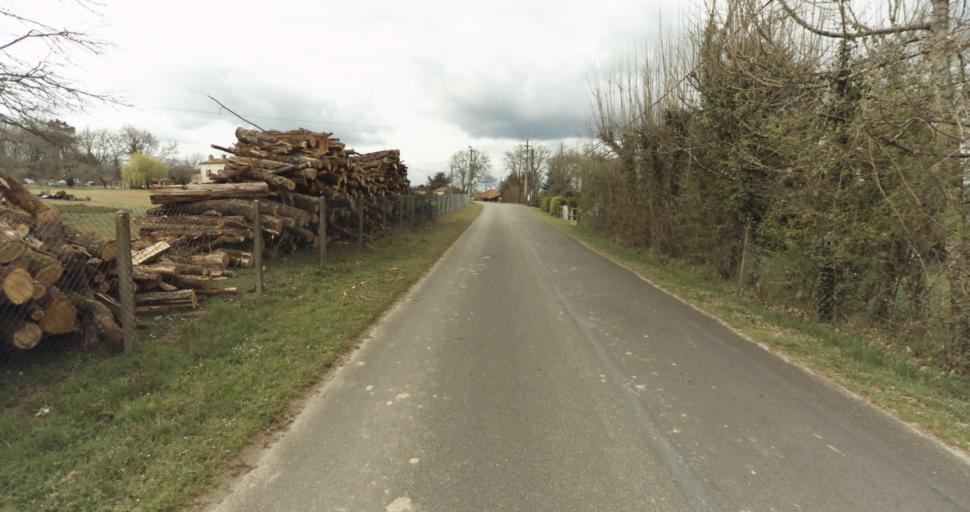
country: FR
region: Aquitaine
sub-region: Departement des Landes
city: Roquefort
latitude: 44.0385
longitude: -0.3284
